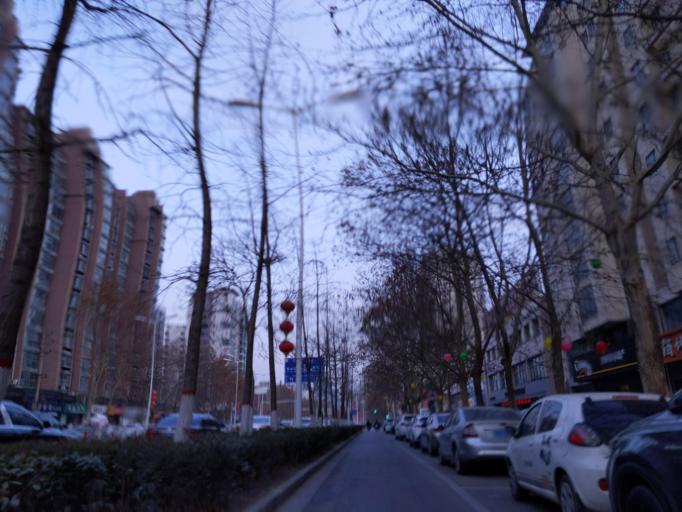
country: CN
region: Henan Sheng
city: Puyang
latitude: 35.7806
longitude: 115.0312
